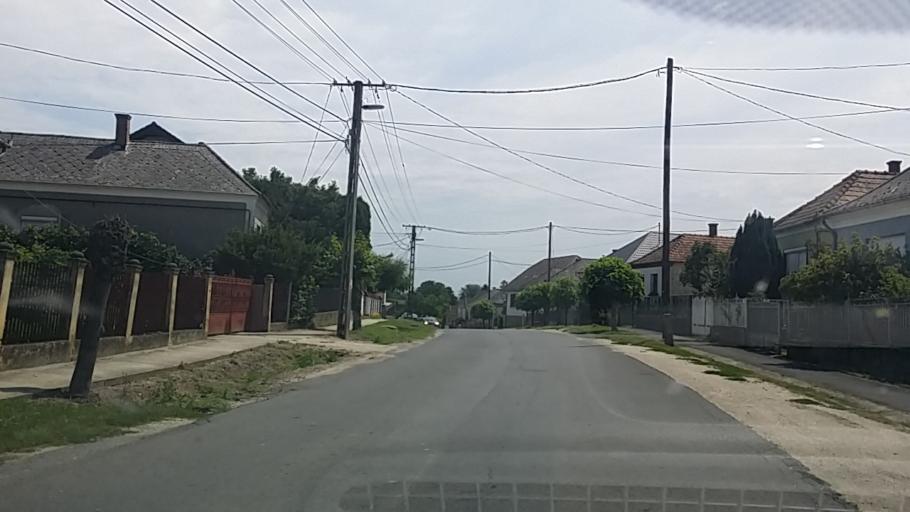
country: HR
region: Medimurska
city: Kotoriba
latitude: 46.3984
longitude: 16.7975
